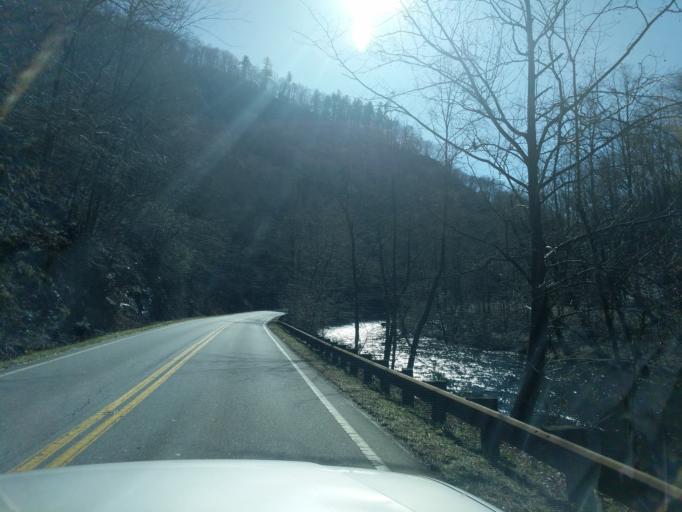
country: US
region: North Carolina
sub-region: Graham County
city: Robbinsville
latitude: 35.3317
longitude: -83.6277
